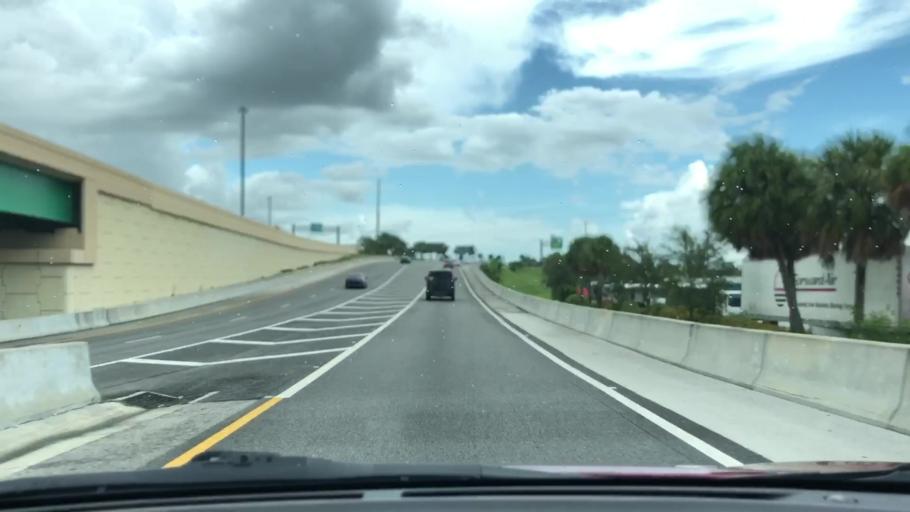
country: US
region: Florida
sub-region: Broward County
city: Broadview Park
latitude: 26.0858
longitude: -80.2134
